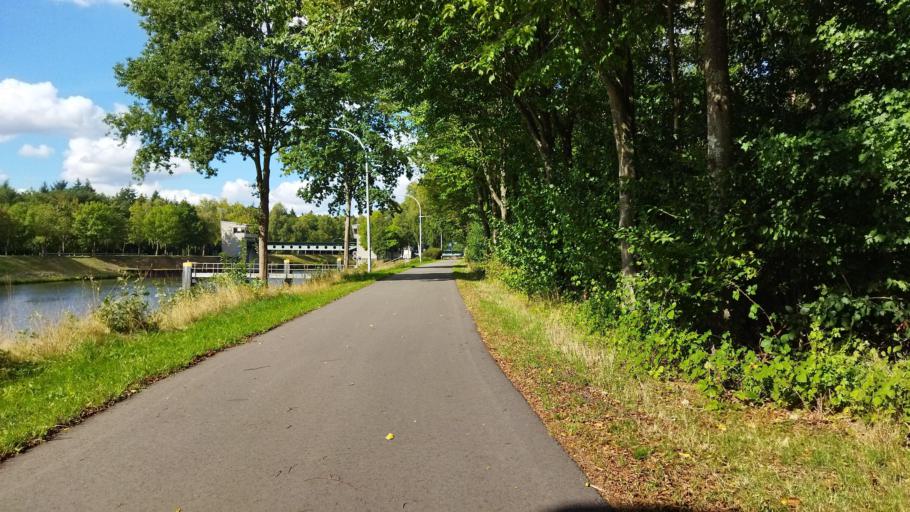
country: DE
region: Lower Saxony
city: Lingen
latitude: 52.4729
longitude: 7.3048
